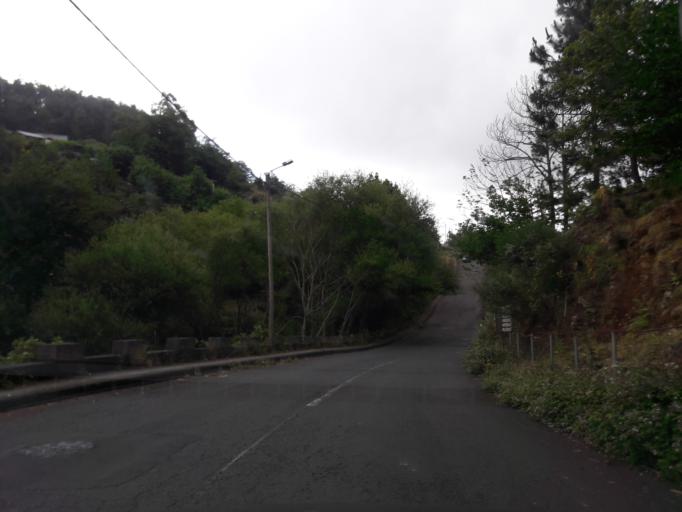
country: PT
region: Madeira
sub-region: Santa Cruz
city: Camacha
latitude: 32.6917
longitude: -16.8683
